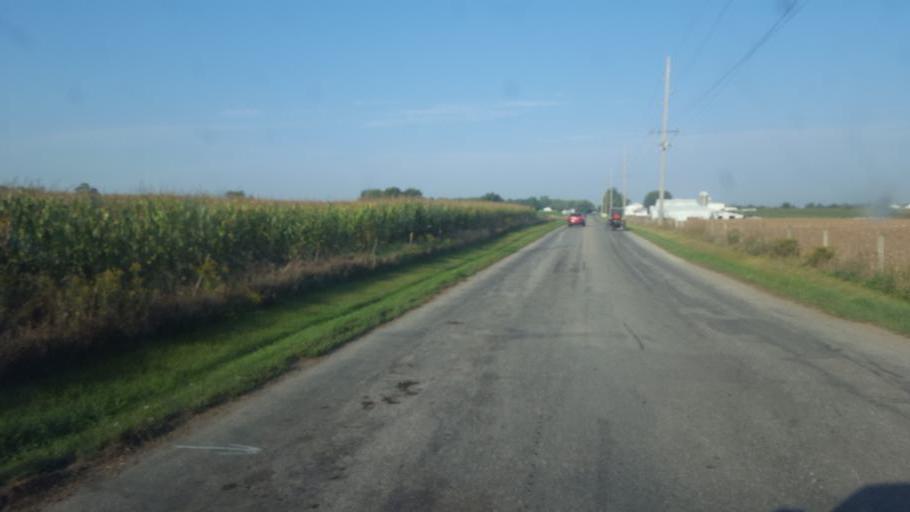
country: US
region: Indiana
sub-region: LaGrange County
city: Topeka
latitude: 41.6767
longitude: -85.5566
